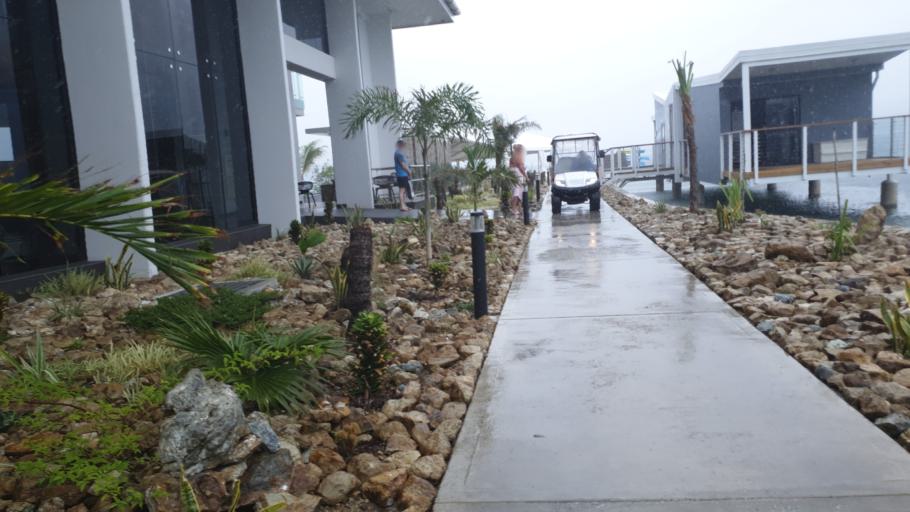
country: PG
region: National Capital
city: Port Moresby
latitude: -9.5348
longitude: 147.2904
